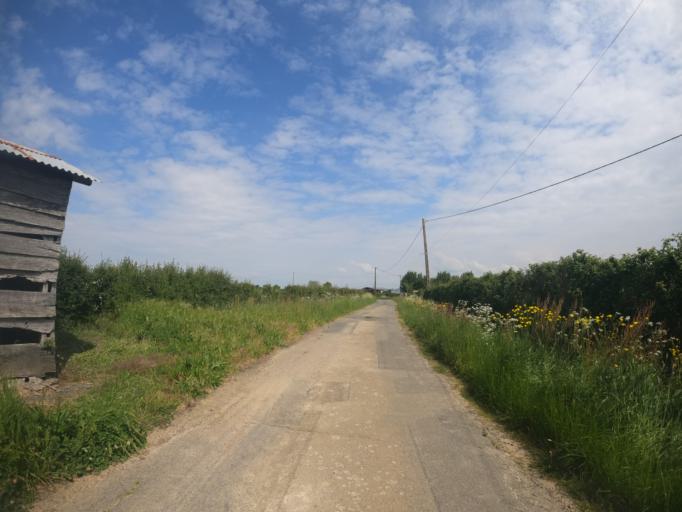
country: FR
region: Poitou-Charentes
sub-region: Departement des Deux-Sevres
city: Saint-Varent
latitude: 46.8888
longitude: -0.2813
